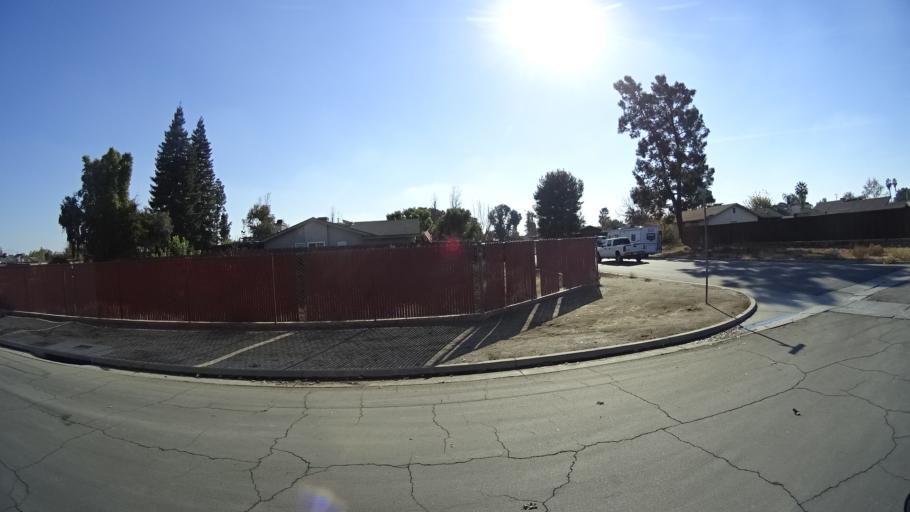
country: US
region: California
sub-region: Kern County
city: Greenfield
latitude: 35.3054
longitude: -119.0520
